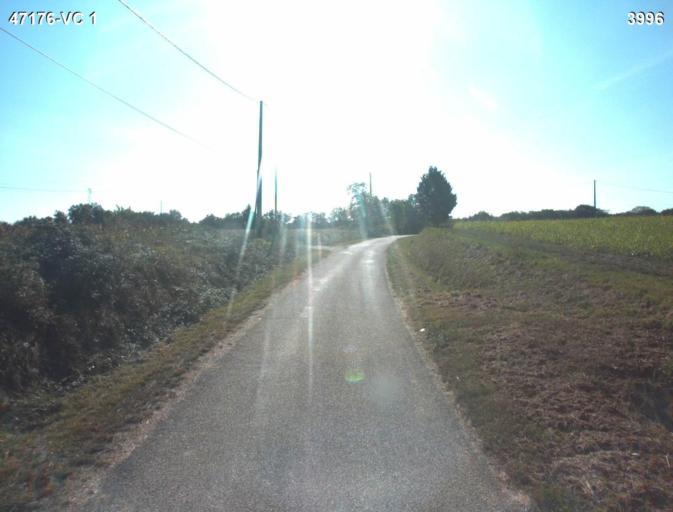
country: FR
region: Aquitaine
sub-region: Departement du Lot-et-Garonne
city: Vianne
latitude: 44.2213
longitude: 0.3116
